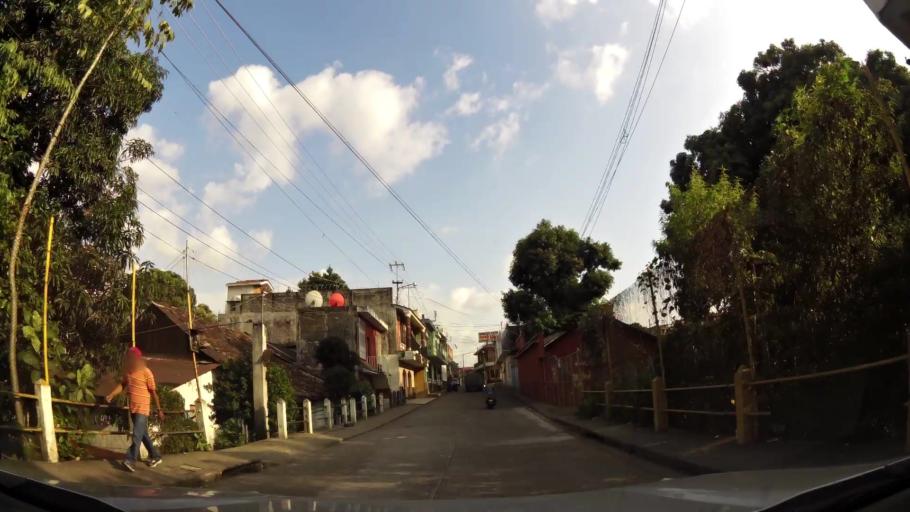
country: GT
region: Retalhuleu
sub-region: Municipio de Retalhuleu
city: Retalhuleu
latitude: 14.5369
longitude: -91.6765
